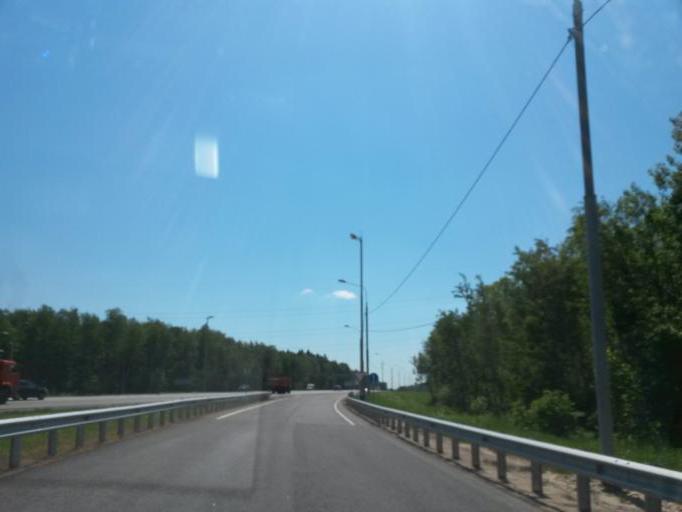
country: RU
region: Moskovskaya
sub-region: Chekhovskiy Rayon
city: Chekhov
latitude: 55.1839
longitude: 37.5343
